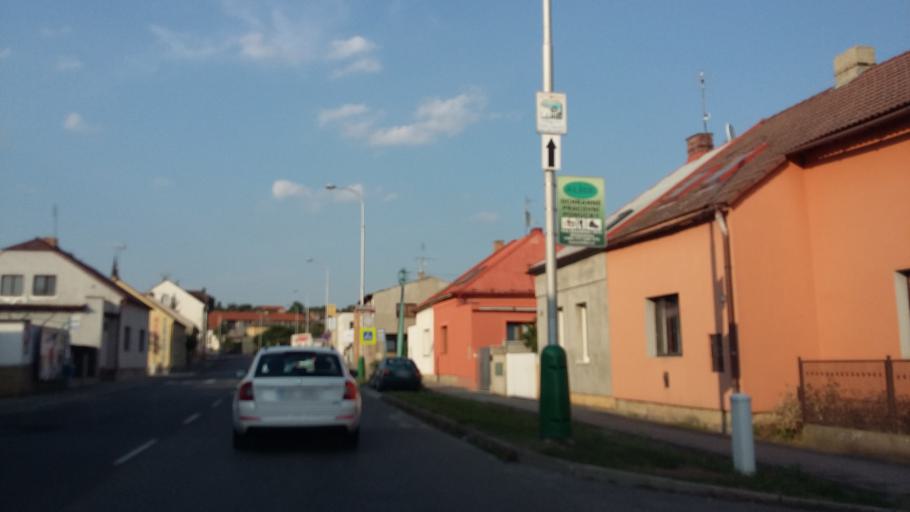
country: CZ
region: Central Bohemia
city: Kosmonosy
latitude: 50.4348
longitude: 14.9280
